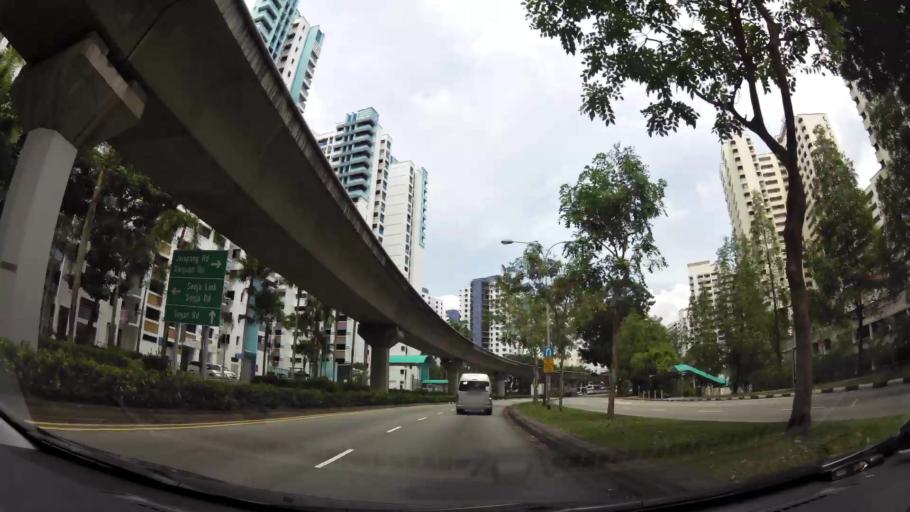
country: MY
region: Johor
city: Johor Bahru
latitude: 1.3847
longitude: 103.7625
